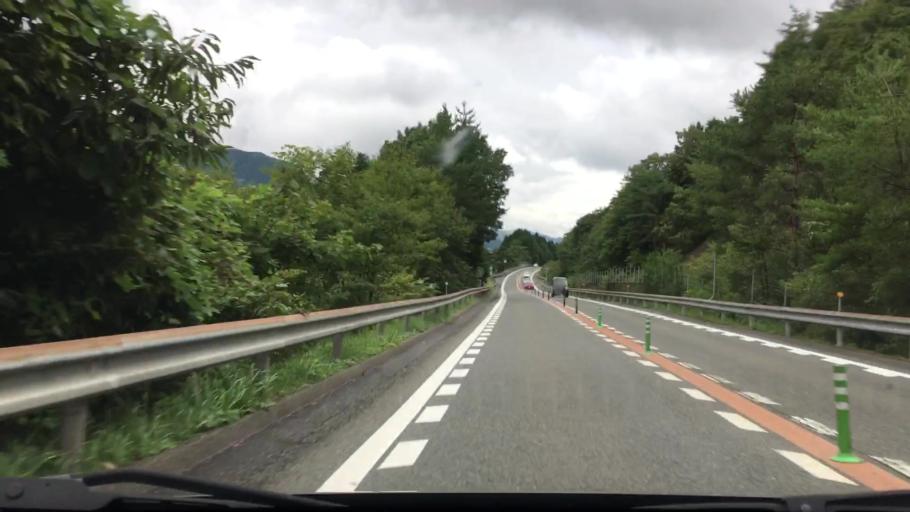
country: JP
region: Hyogo
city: Nishiwaki
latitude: 35.0748
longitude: 134.7705
